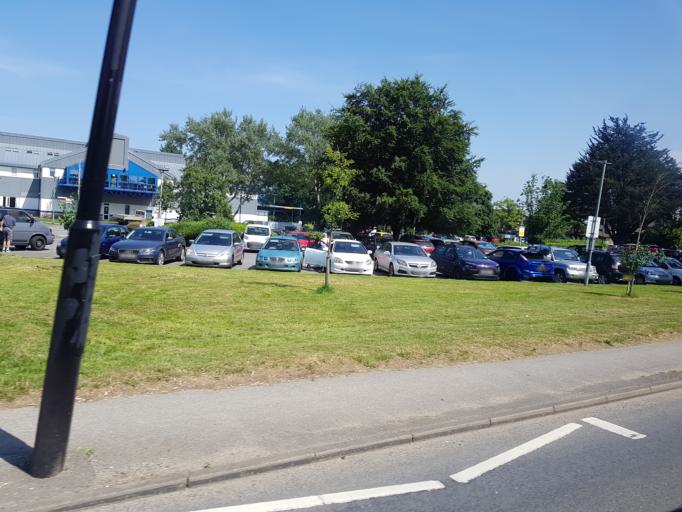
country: GB
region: England
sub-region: Isle of Wight
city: Newport
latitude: 50.7106
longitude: -1.3028
